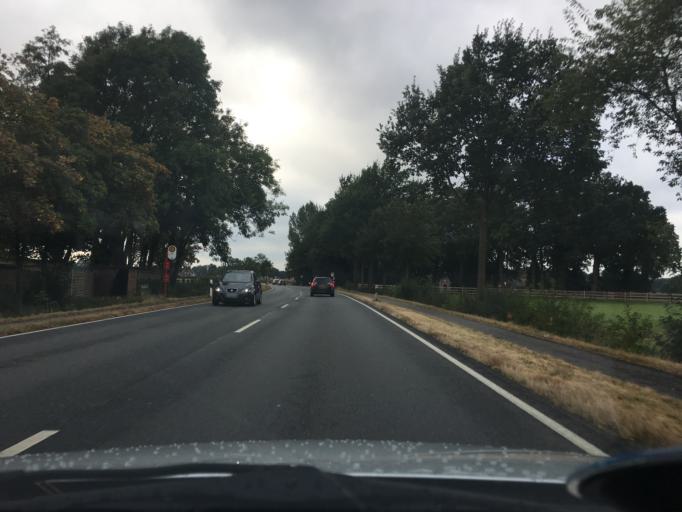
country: DE
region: Lower Saxony
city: Alfhausen
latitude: 52.4907
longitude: 7.9575
